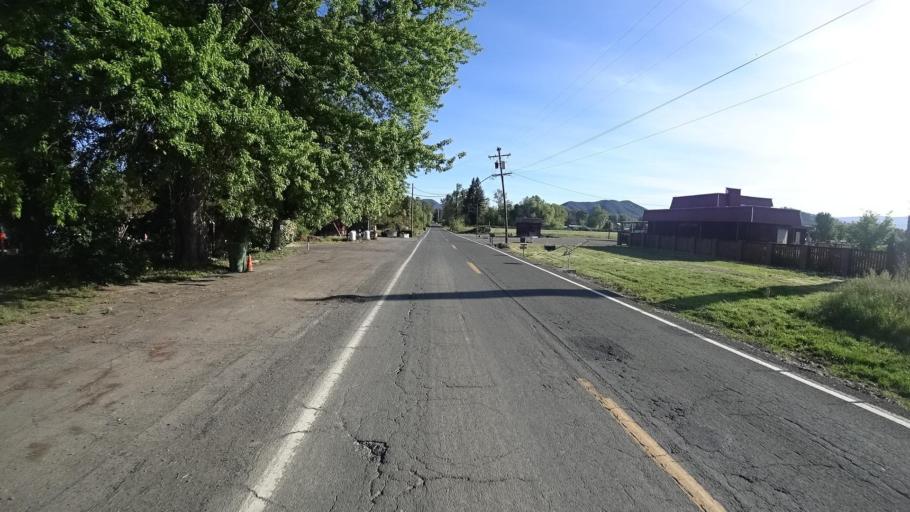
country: US
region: California
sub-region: Lake County
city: North Lakeport
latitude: 39.0814
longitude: -122.9498
